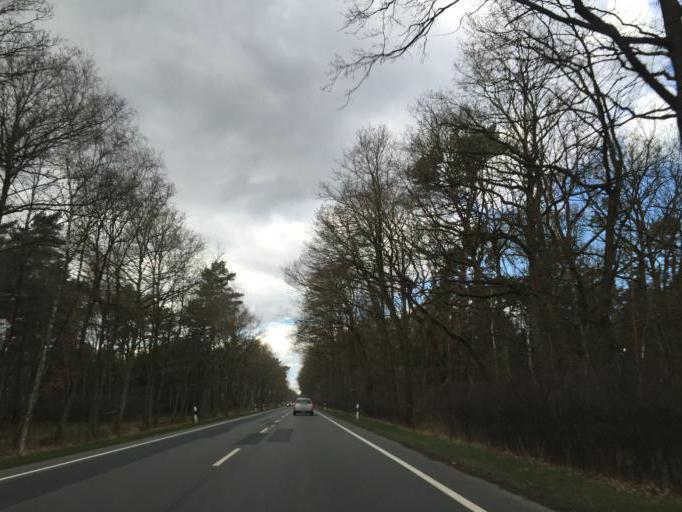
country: DE
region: Lower Saxony
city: Broeckel
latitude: 52.4850
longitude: 10.2546
